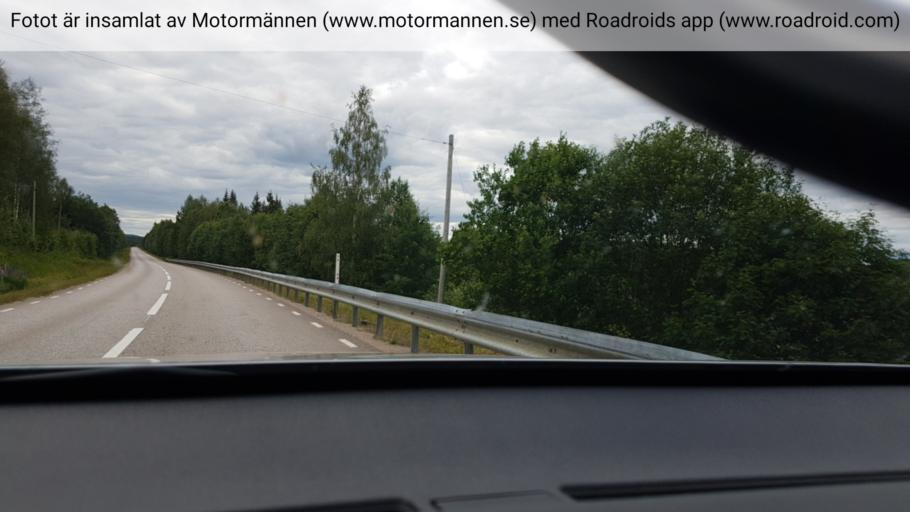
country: NO
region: Hedmark
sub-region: Trysil
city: Innbygda
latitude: 60.9170
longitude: 12.5403
